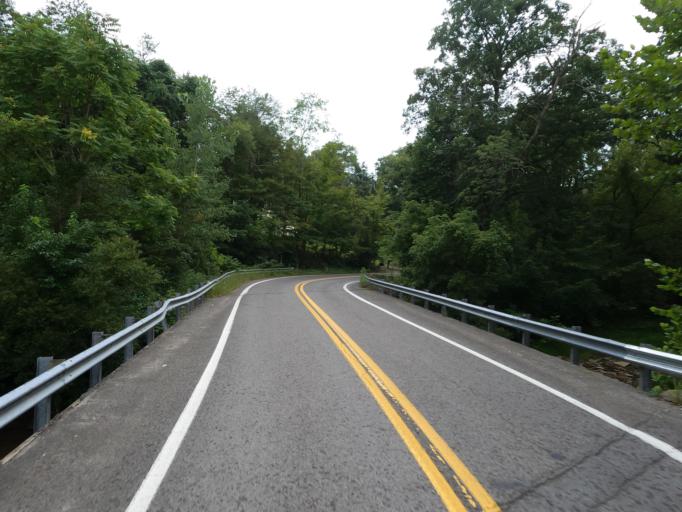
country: US
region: West Virginia
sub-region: Marion County
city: Fairmont
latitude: 39.5095
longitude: -80.1003
